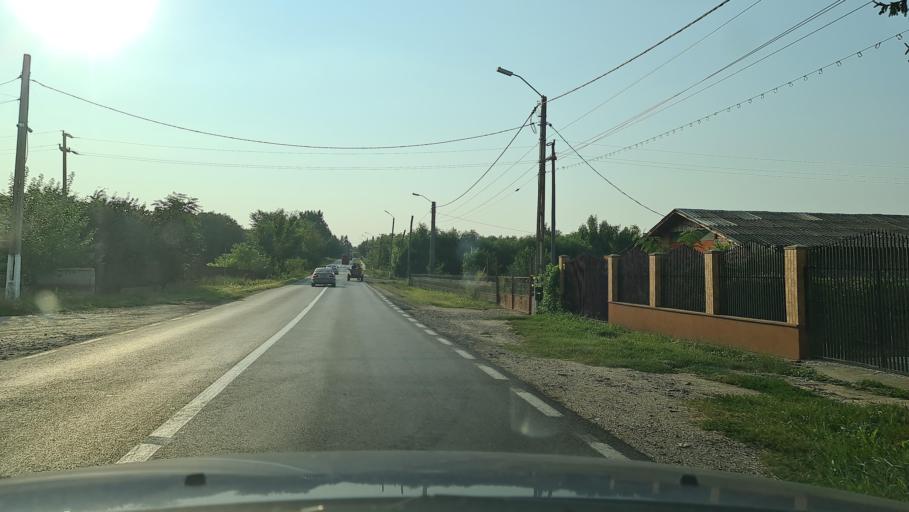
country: RO
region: Calarasi
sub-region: Comuna Dor Marunt
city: Dor Marunt
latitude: 44.4452
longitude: 26.9276
